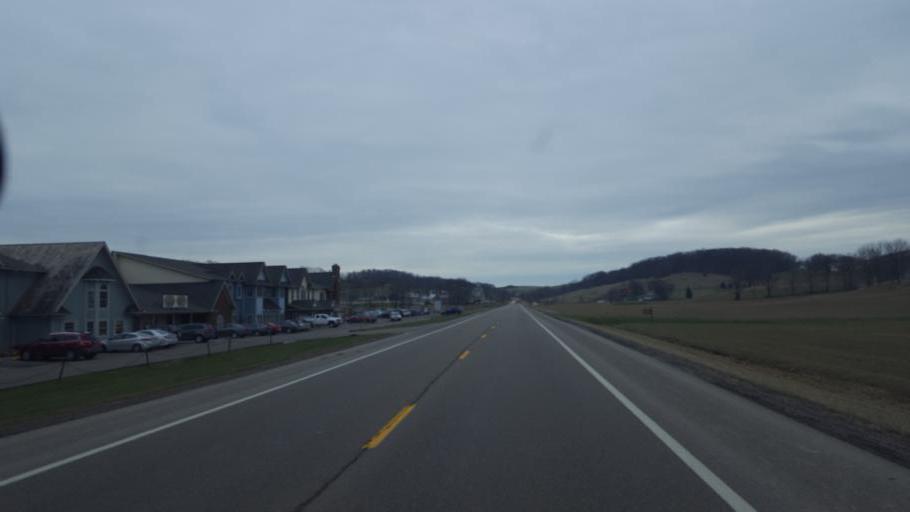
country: US
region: Ohio
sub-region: Tuscarawas County
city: Sugarcreek
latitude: 40.5289
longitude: -81.7182
